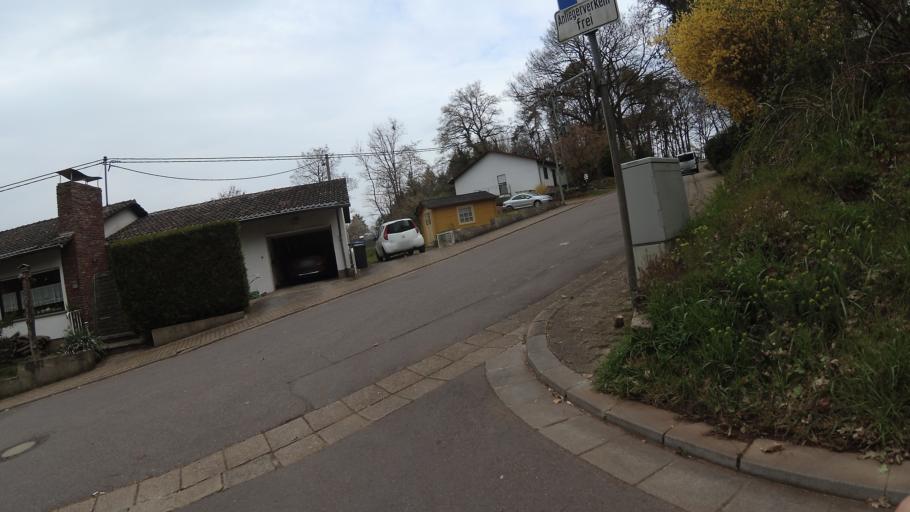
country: DE
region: Saarland
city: Merzig
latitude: 49.4623
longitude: 6.6251
